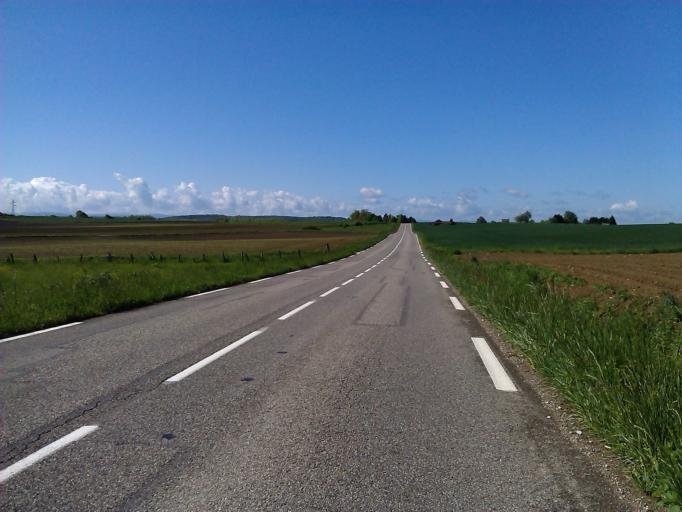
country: FR
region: Alsace
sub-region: Departement du Haut-Rhin
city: Heimsbrunn
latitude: 47.6928
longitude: 7.2205
